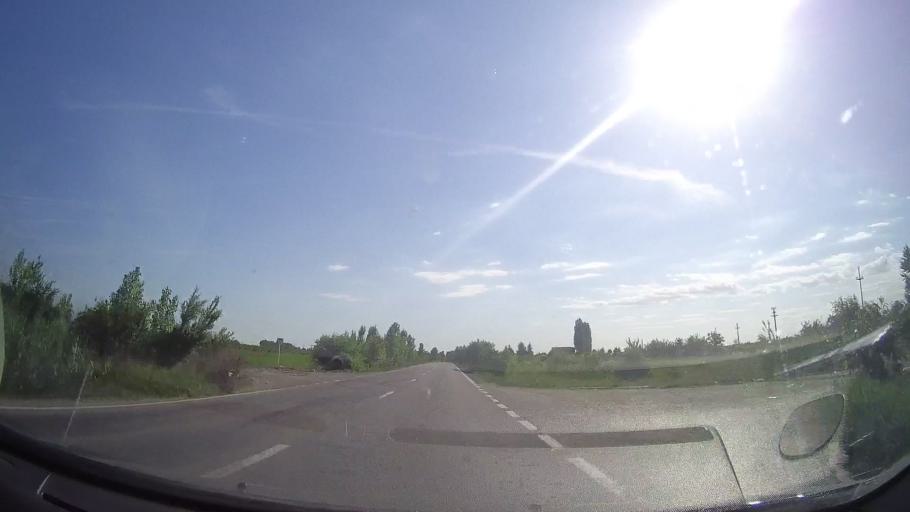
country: RO
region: Prahova
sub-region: Comuna Barcanesti
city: Barcanesti
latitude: 44.8962
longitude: 26.0562
